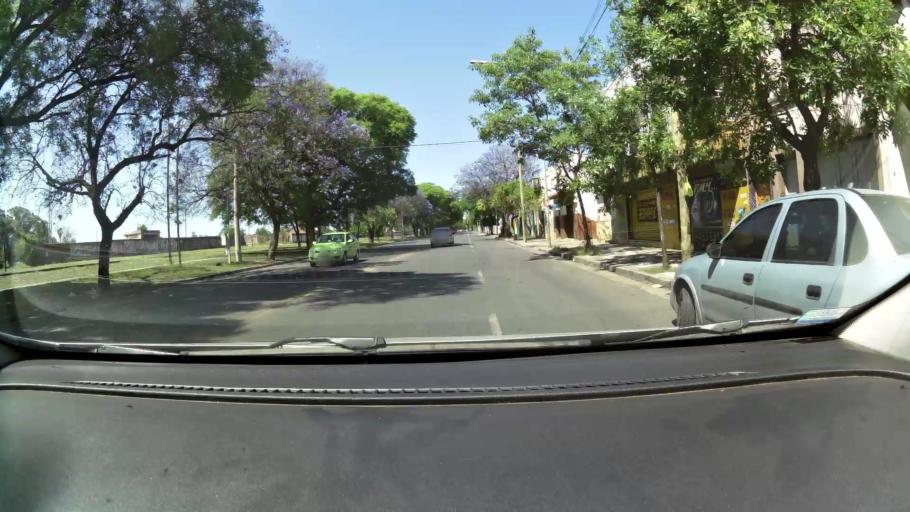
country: AR
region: Cordoba
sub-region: Departamento de Capital
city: Cordoba
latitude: -31.3986
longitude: -64.1674
